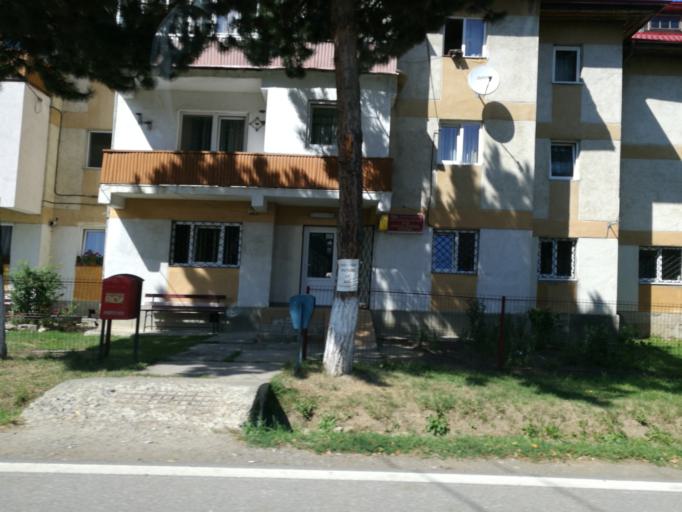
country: RO
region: Suceava
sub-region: Comuna Putna
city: Putna
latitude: 47.8706
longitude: 25.6109
